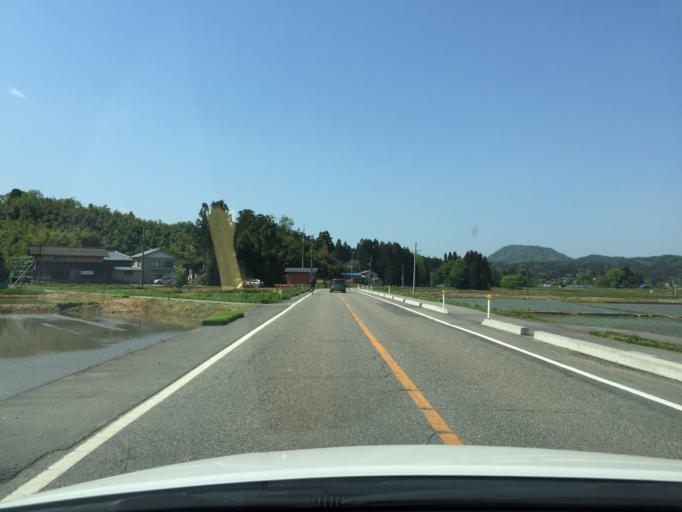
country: JP
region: Niigata
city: Muramatsu
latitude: 37.6707
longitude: 139.1463
